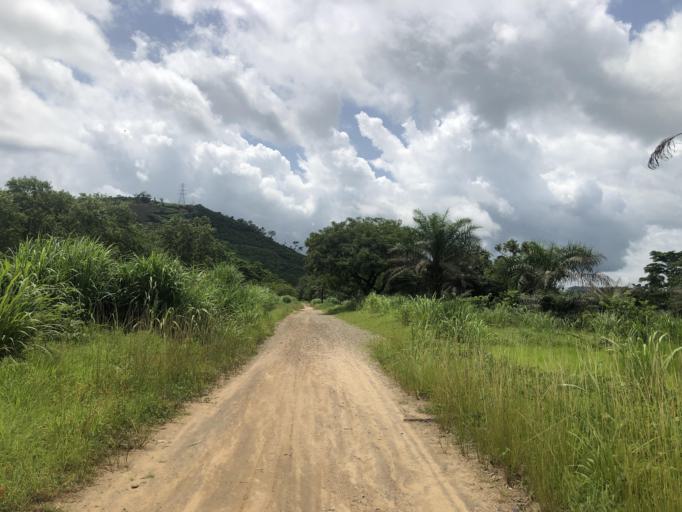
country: SL
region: Northern Province
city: Bumbuna
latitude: 9.0107
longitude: -11.7678
